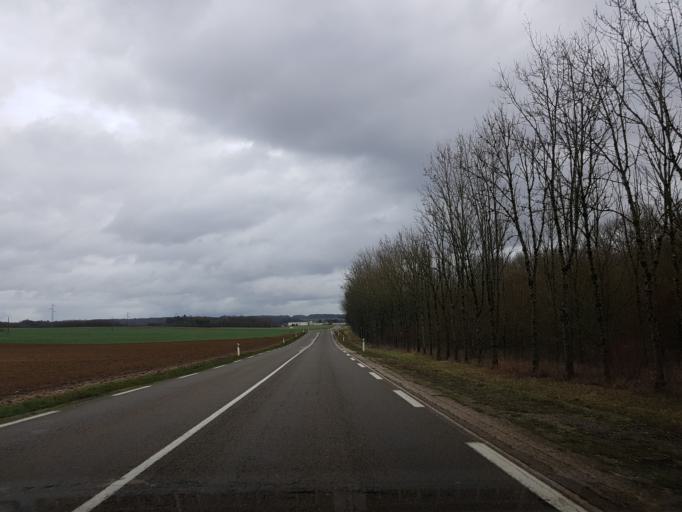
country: FR
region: Franche-Comte
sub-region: Departement de la Haute-Saone
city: Jussey
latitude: 47.7194
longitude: 5.8681
